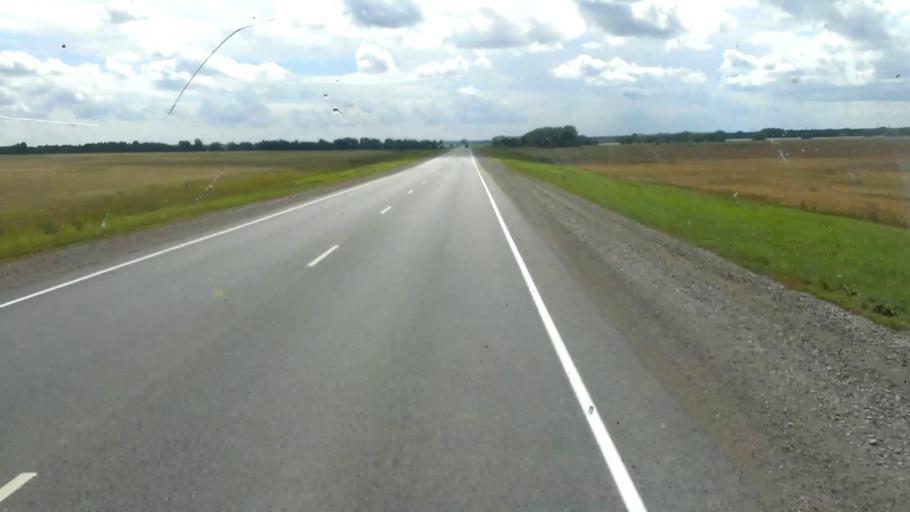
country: RU
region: Altai Krai
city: Troitskoye
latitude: 52.8988
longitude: 84.8332
